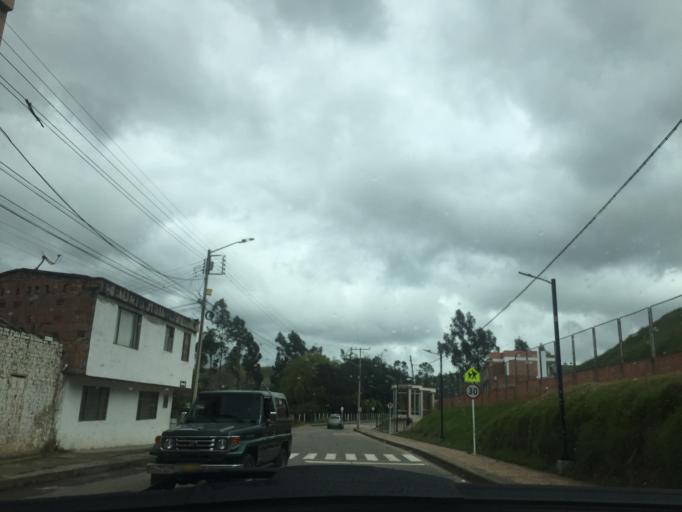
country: CO
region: Cundinamarca
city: Villapinzon
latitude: 5.2191
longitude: -73.5943
